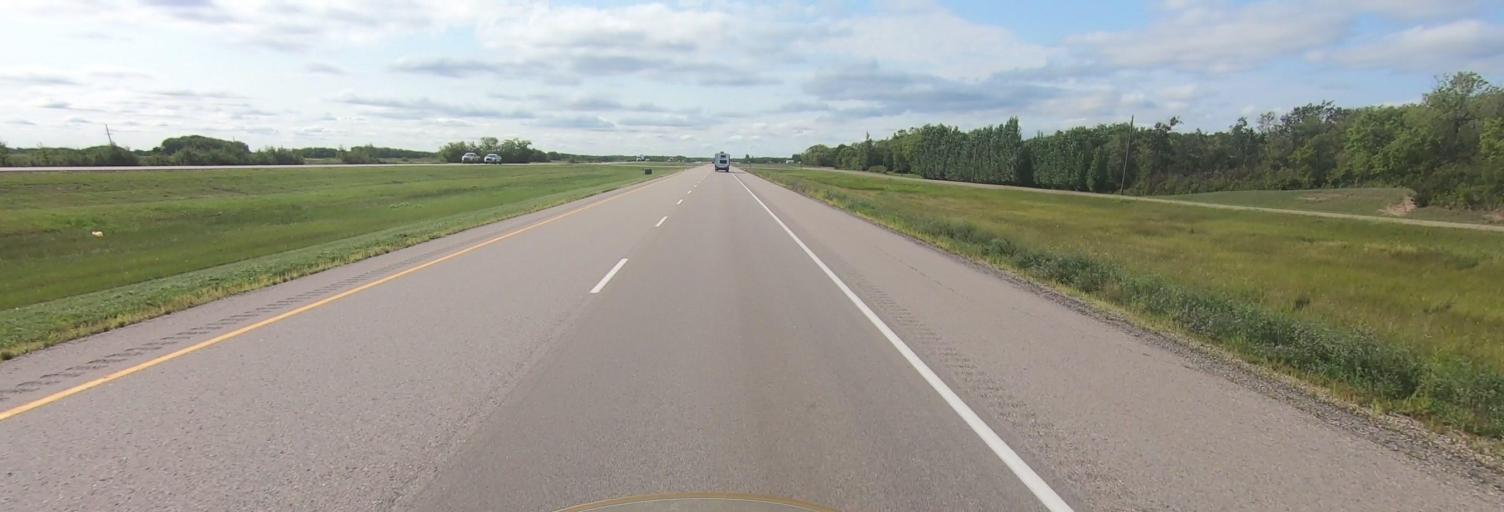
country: CA
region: Manitoba
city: Virden
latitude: 49.7943
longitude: -100.8000
